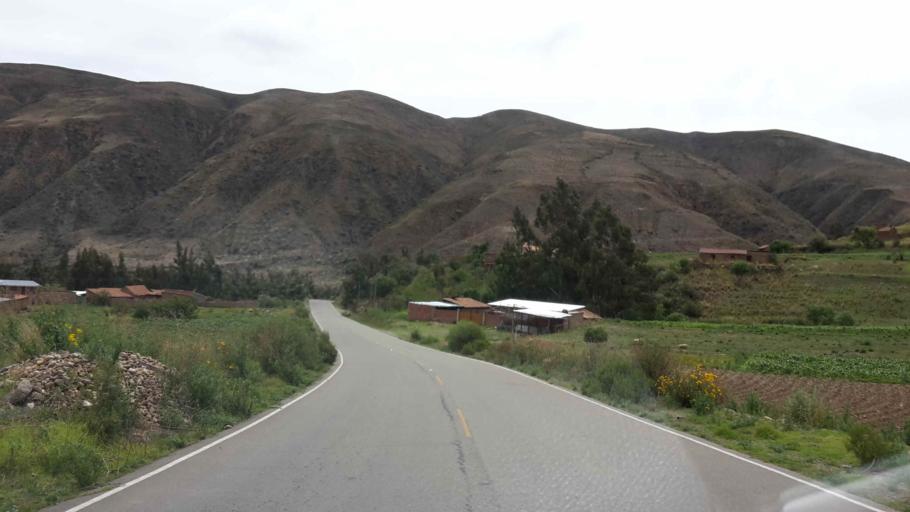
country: BO
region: Cochabamba
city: Colomi
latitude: -17.4093
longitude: -65.7810
